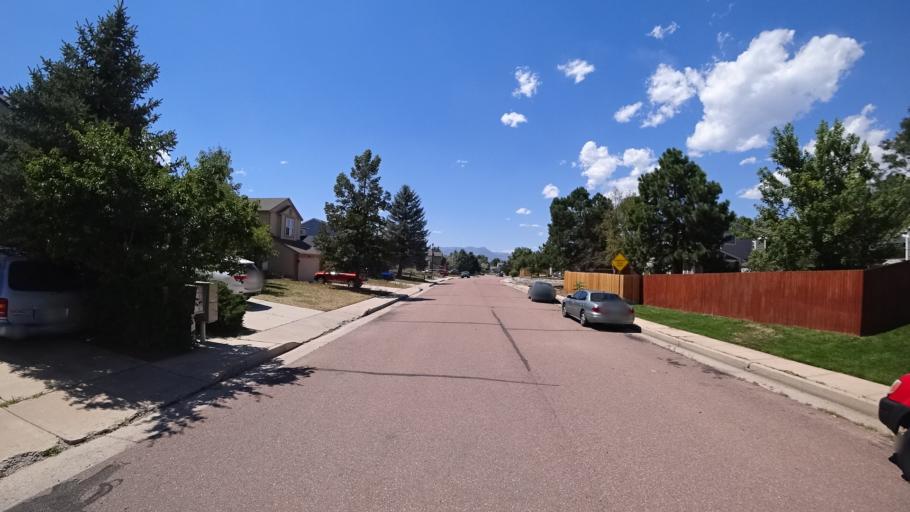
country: US
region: Colorado
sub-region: El Paso County
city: Black Forest
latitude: 38.9525
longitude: -104.7481
